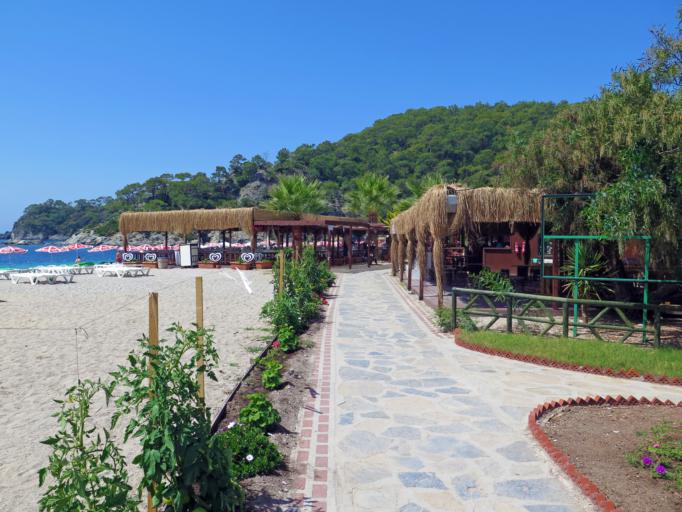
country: TR
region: Mugla
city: OEluedeniz
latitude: 36.5501
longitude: 29.1164
